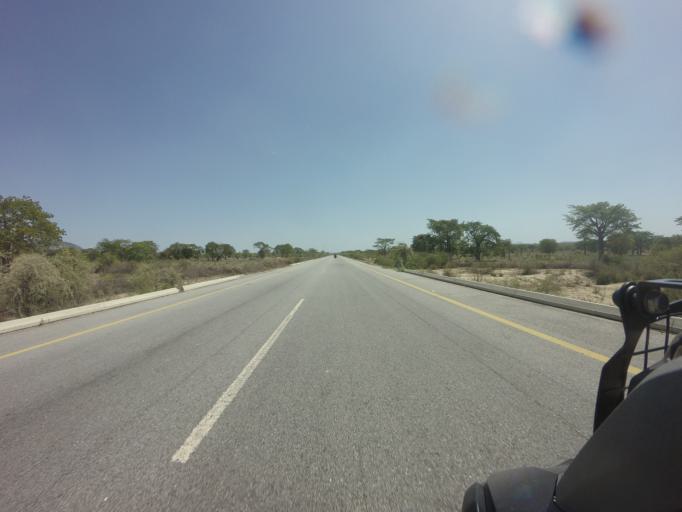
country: AO
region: Benguela
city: Benguela
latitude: -13.1742
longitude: 13.7641
